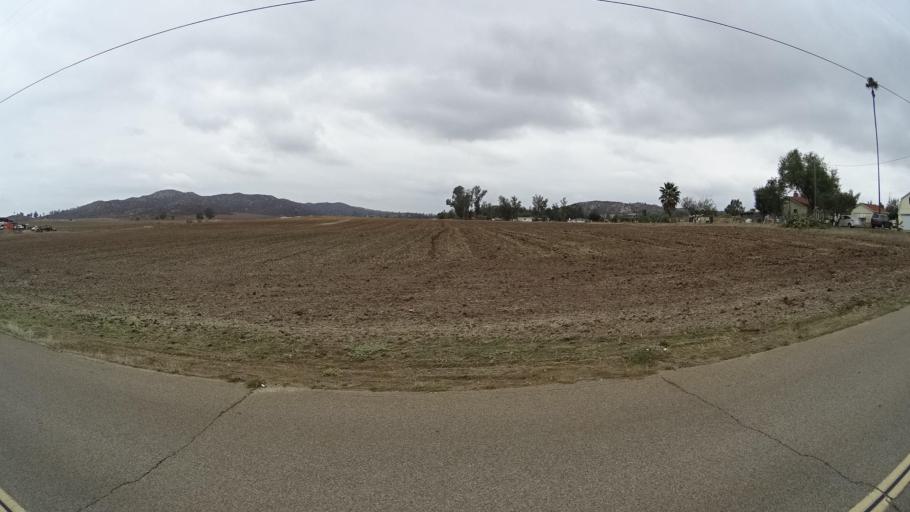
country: US
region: California
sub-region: San Diego County
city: Ramona
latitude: 33.0405
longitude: -116.9063
